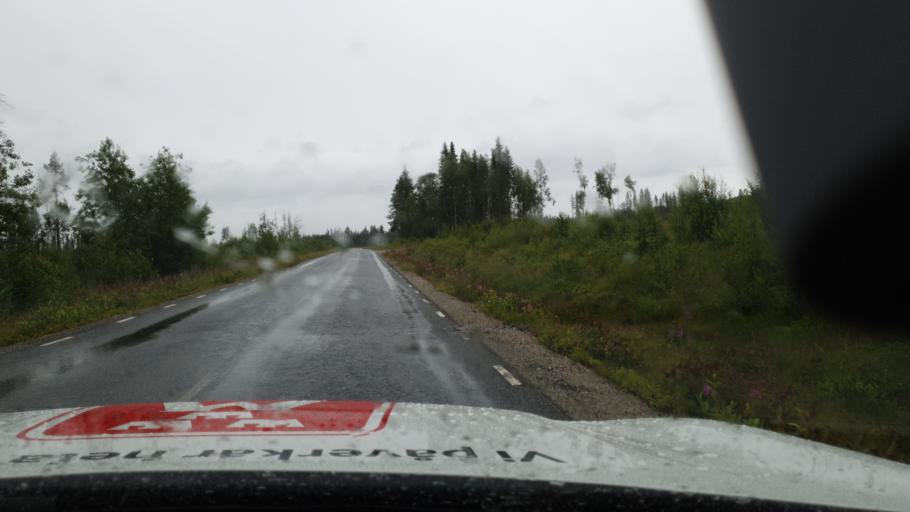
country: SE
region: Vaesterbotten
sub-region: Vindelns Kommun
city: Vindeln
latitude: 64.4682
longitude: 19.7613
